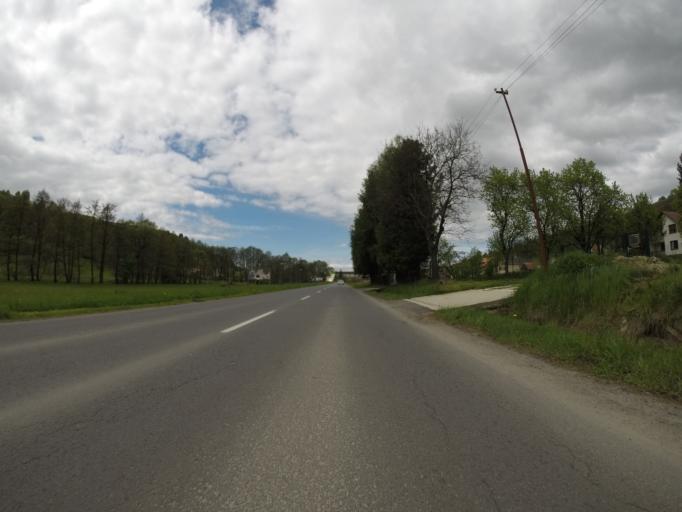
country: SK
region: Banskobystricky
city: Hrinova
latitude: 48.5718
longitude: 19.5128
